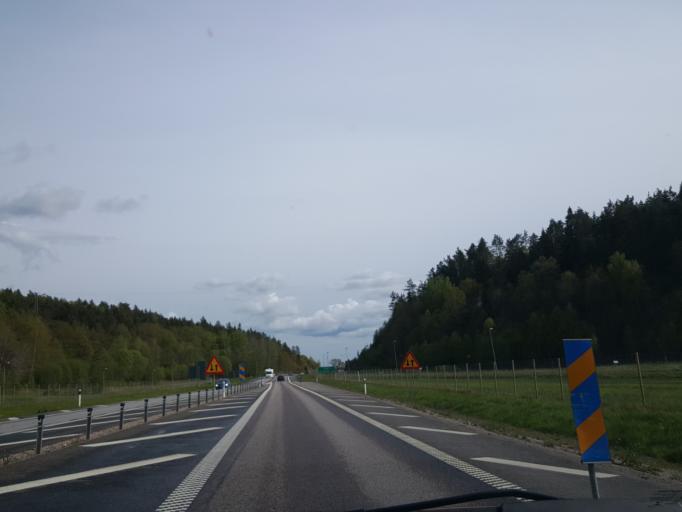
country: SE
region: Vaestra Goetaland
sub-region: Lilla Edets Kommun
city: Lilla Edet
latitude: 58.1168
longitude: 12.1411
